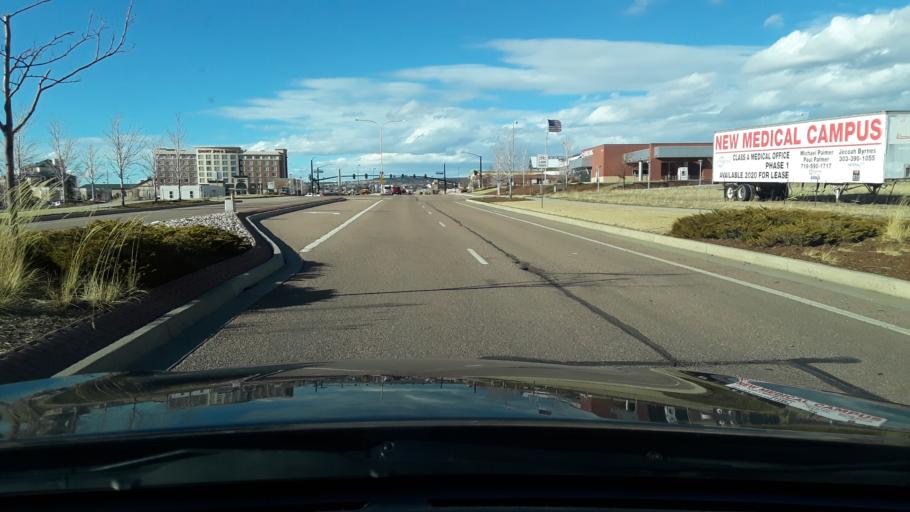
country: US
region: Colorado
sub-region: El Paso County
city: Air Force Academy
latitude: 38.9890
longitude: -104.8077
